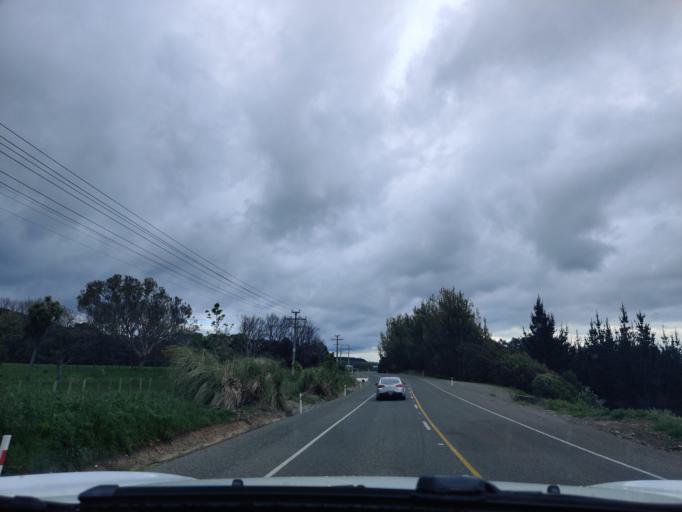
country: NZ
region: Manawatu-Wanganui
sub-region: Palmerston North City
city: Palmerston North
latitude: -40.3338
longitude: 175.7311
